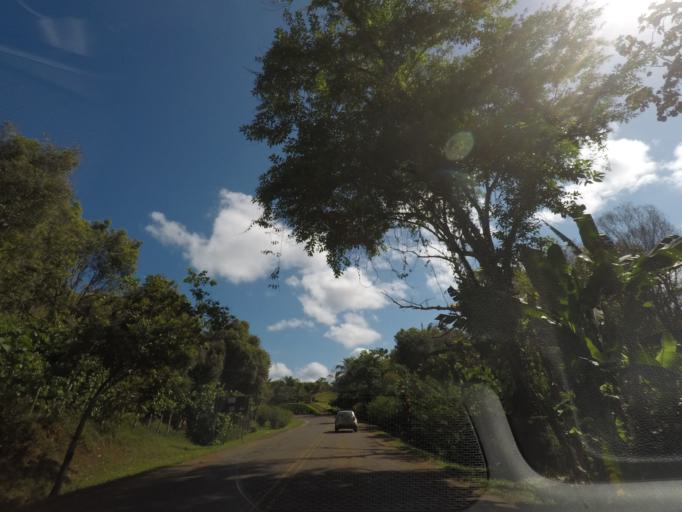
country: BR
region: Bahia
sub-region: Camamu
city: Camamu
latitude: -13.8937
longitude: -39.1387
